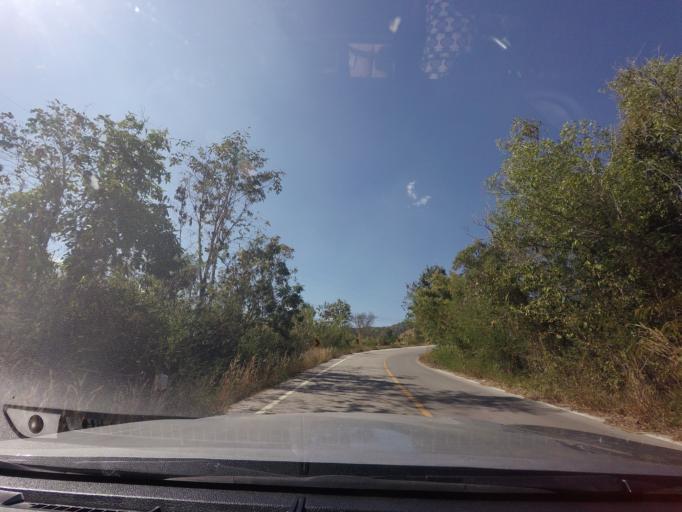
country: TH
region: Lampang
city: Chae Hom
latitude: 18.6196
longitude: 99.6237
